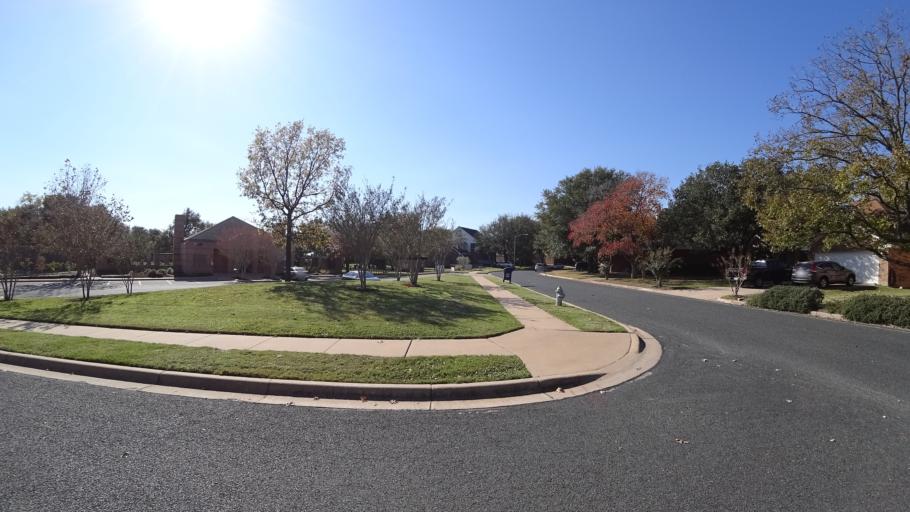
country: US
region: Texas
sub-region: Travis County
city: Shady Hollow
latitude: 30.2220
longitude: -97.8699
